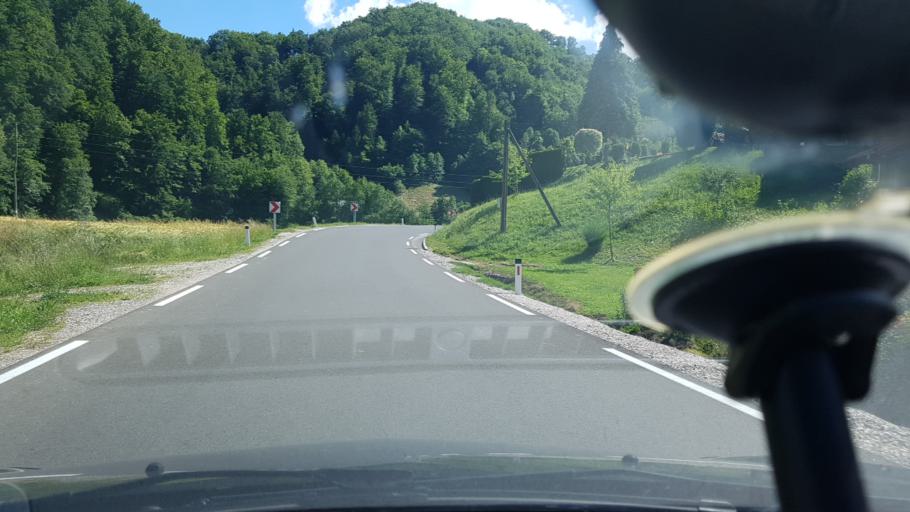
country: SI
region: Zetale
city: Zetale
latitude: 46.2871
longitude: 15.8241
